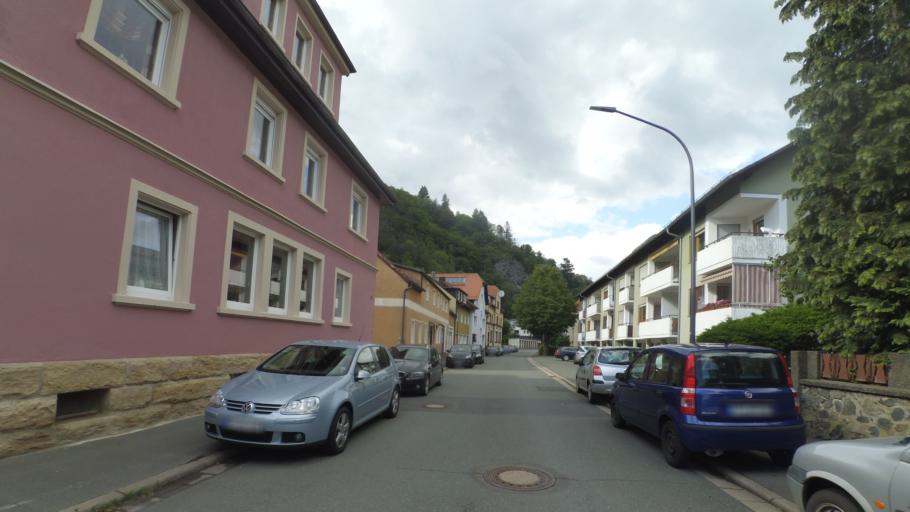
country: DE
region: Bavaria
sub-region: Upper Franconia
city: Bad Berneck im Fichtelgebirge
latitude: 50.0456
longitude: 11.6709
